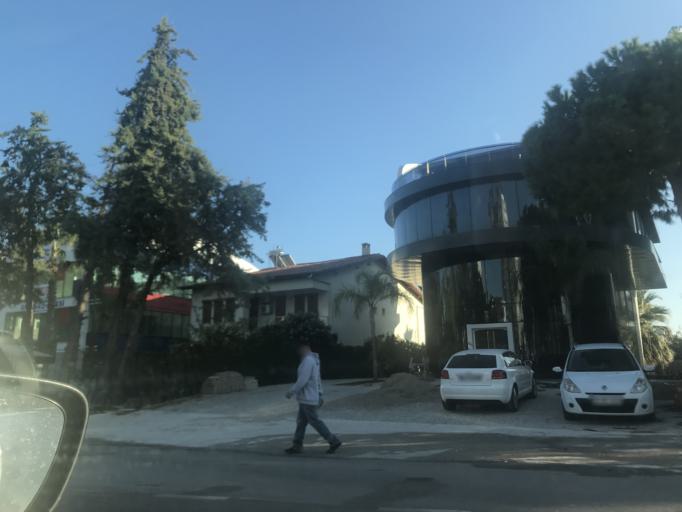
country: TR
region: Antalya
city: Antalya
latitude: 36.8519
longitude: 30.7709
